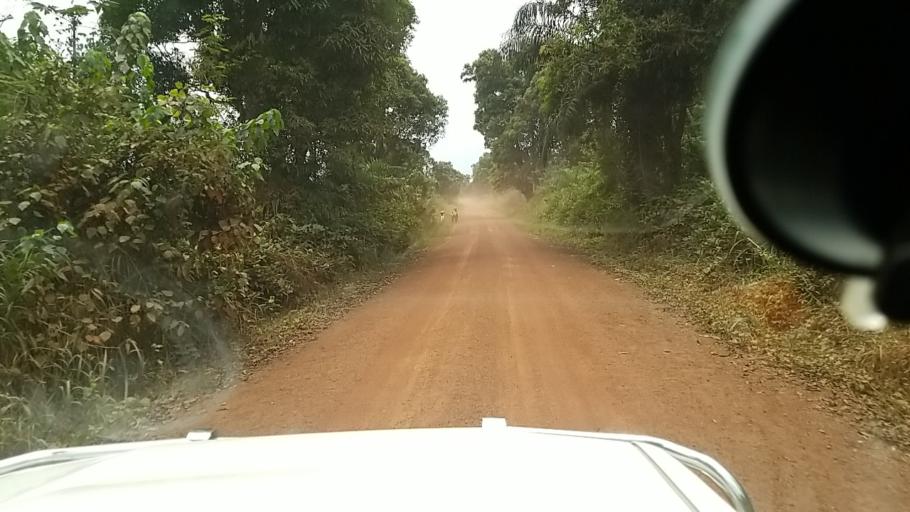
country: CD
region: Equateur
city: Libenge
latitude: 3.7362
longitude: 18.7784
